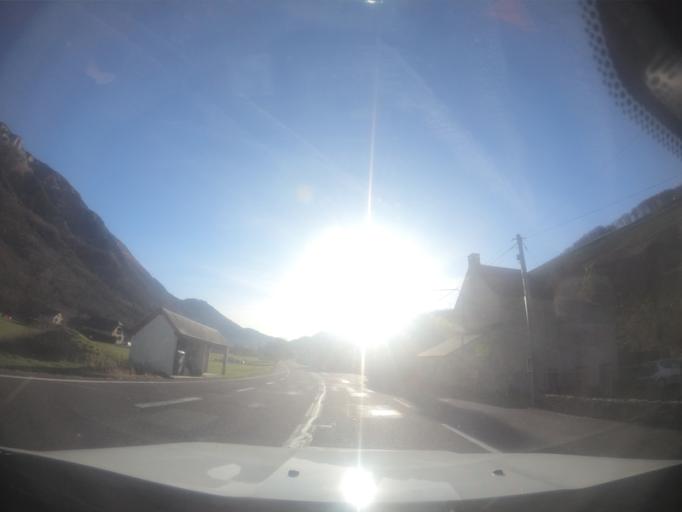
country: FR
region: Midi-Pyrenees
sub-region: Departement des Hautes-Pyrenees
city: Campan
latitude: 43.0046
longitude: 0.1907
